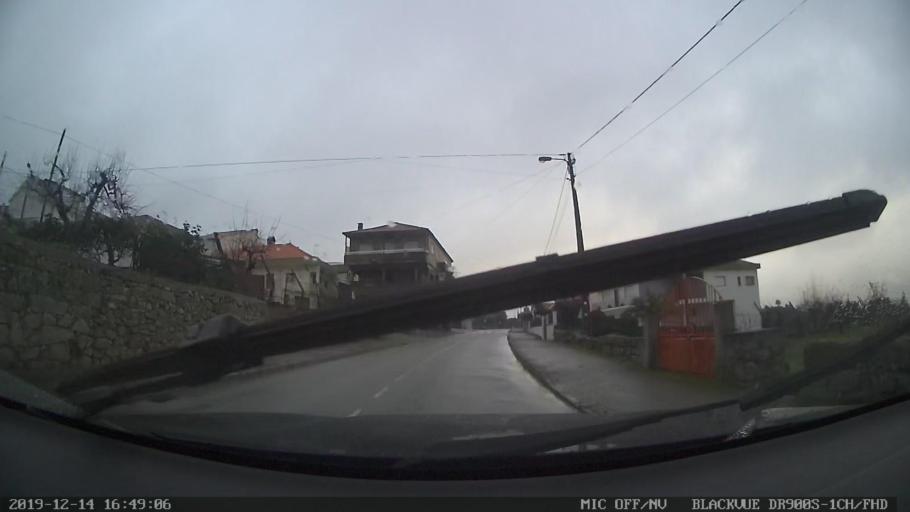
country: PT
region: Vila Real
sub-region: Murca
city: Murca
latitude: 41.4073
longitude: -7.5026
